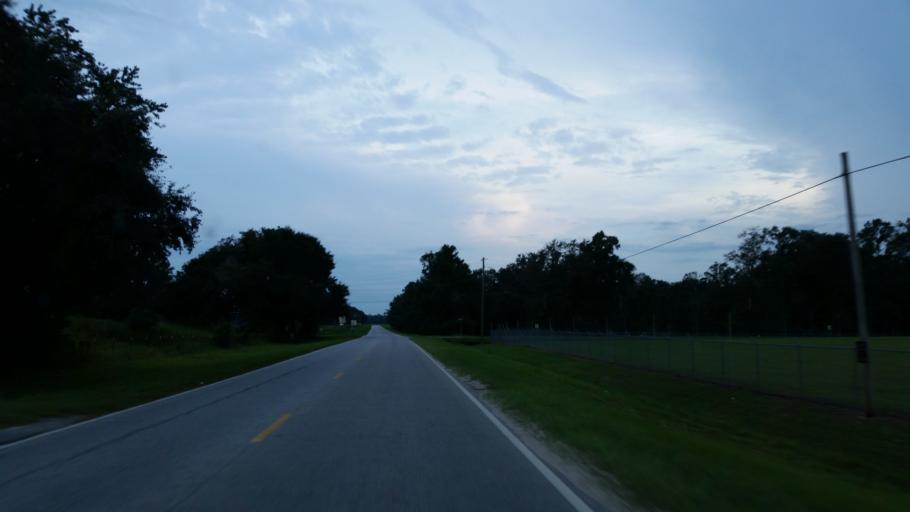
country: US
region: Georgia
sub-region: Echols County
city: Statenville
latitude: 30.6644
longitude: -83.1842
